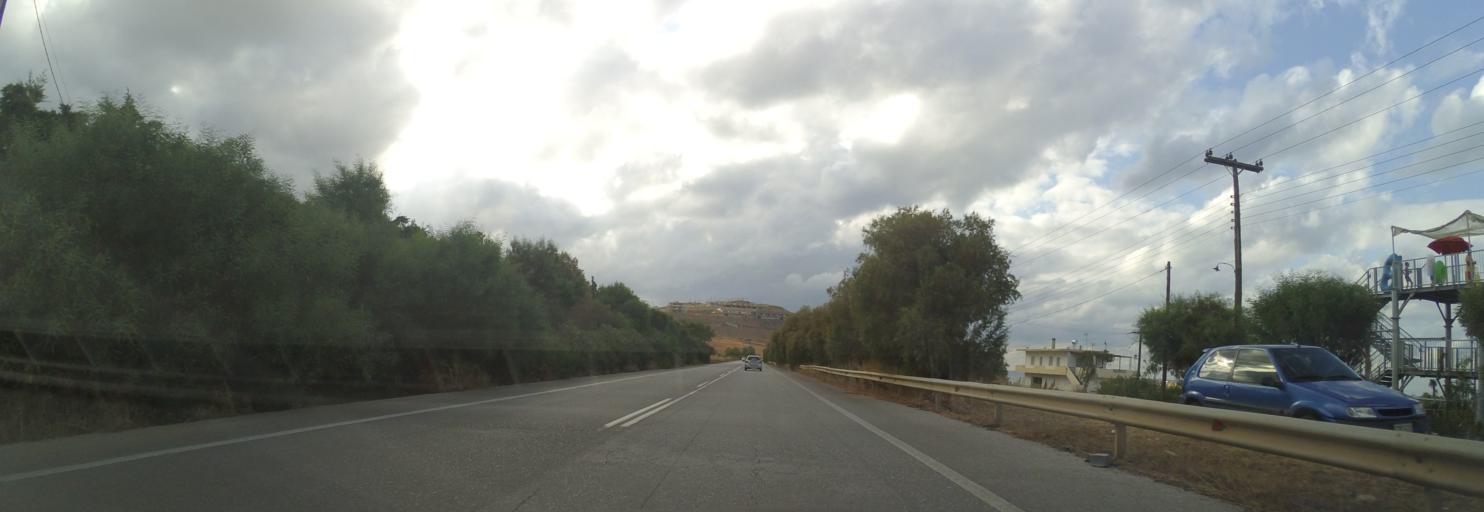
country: GR
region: Crete
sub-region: Nomos Rethymnis
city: Panormos
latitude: 35.4160
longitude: 24.6850
